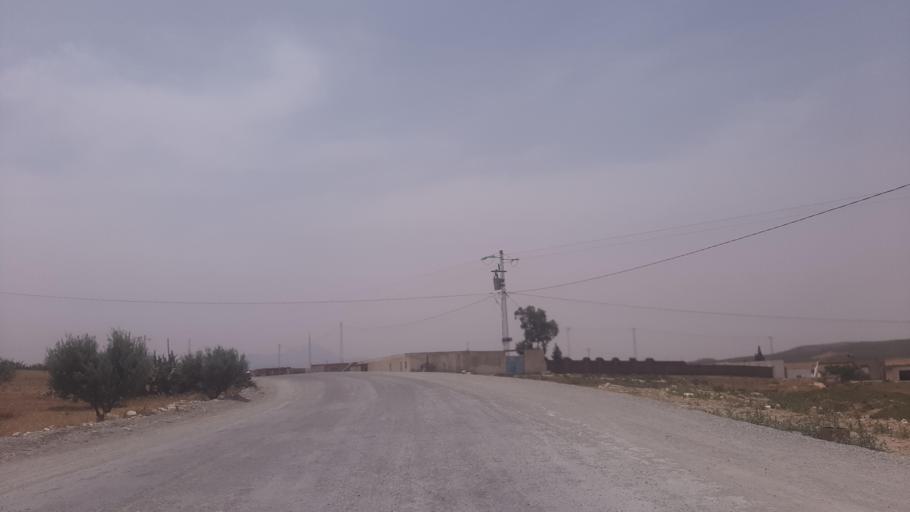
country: TN
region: Zaghwan
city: Zaghouan
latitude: 36.5260
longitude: 10.1589
